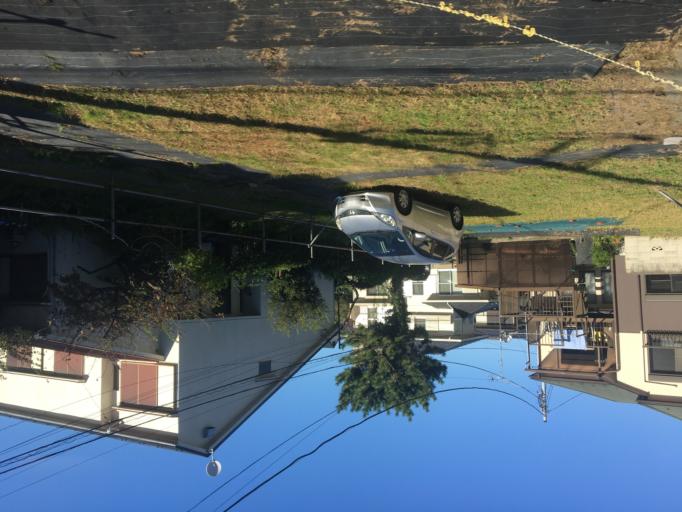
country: JP
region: Chiba
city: Funabashi
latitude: 35.7186
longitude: 139.9408
